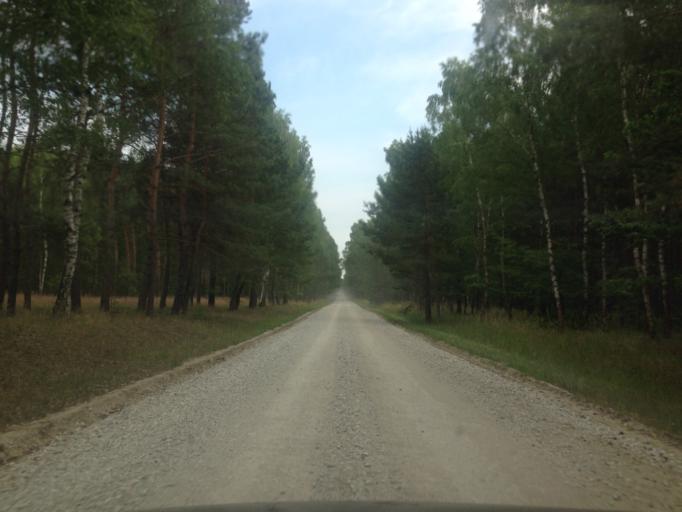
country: PL
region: Kujawsko-Pomorskie
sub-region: Powiat golubsko-dobrzynski
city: Radomin
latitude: 53.1766
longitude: 19.1841
